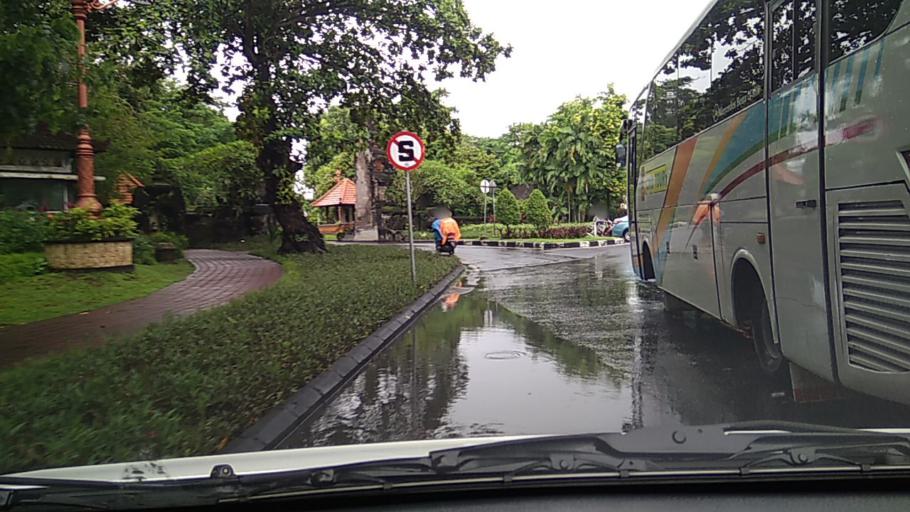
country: ID
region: Bali
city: Bualu
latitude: -8.7893
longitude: 115.2262
